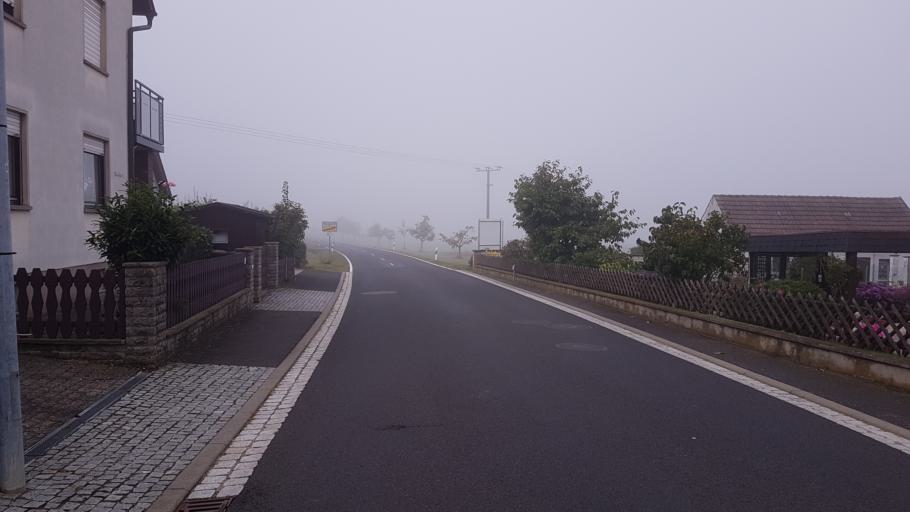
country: DE
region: Bavaria
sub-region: Regierungsbezirk Unterfranken
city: Kolitzheim
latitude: 49.9267
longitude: 10.2000
